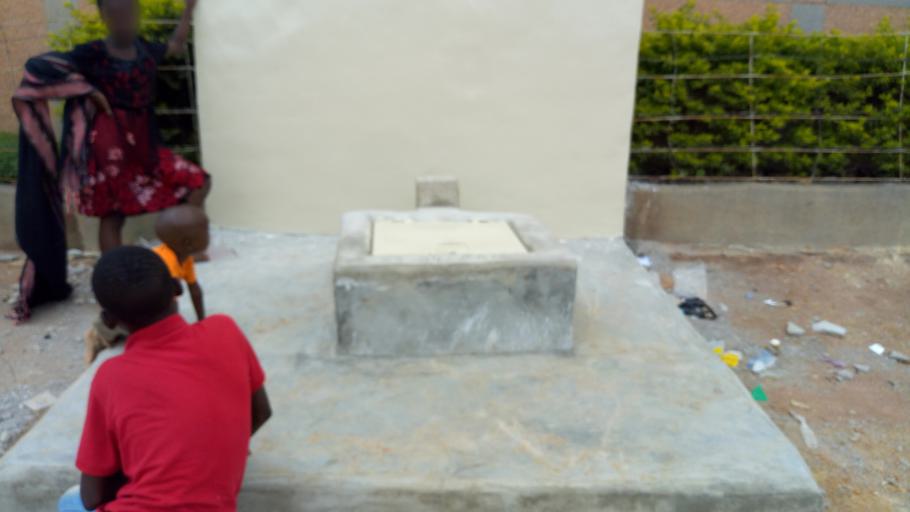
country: CI
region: Vallee du Bandama
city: Bouake
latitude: 7.7019
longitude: -5.0413
